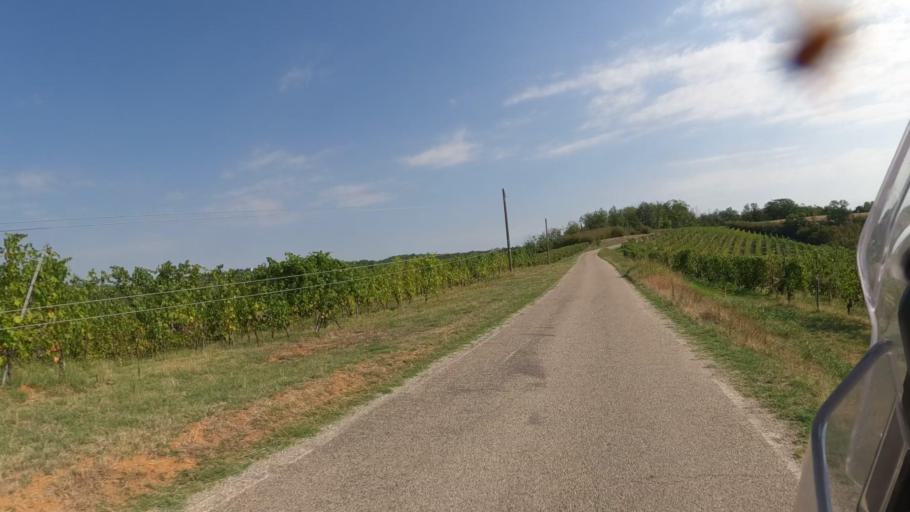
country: IT
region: Piedmont
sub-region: Provincia di Asti
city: Viarigi
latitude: 44.9569
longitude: 8.3738
